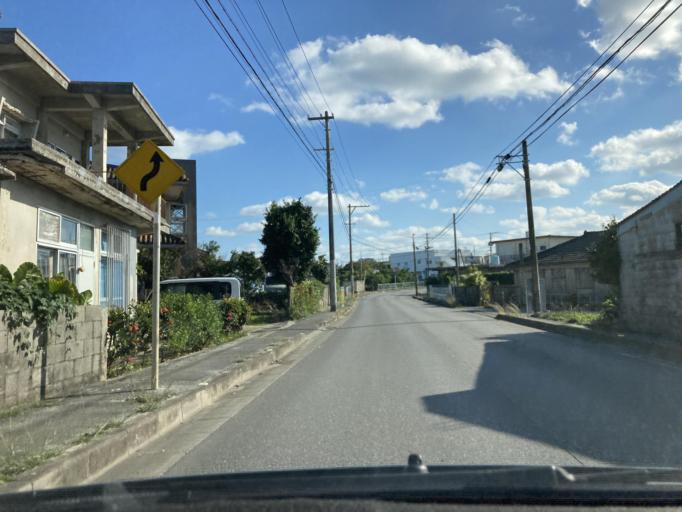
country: JP
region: Okinawa
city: Katsuren-haebaru
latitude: 26.3137
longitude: 127.9101
